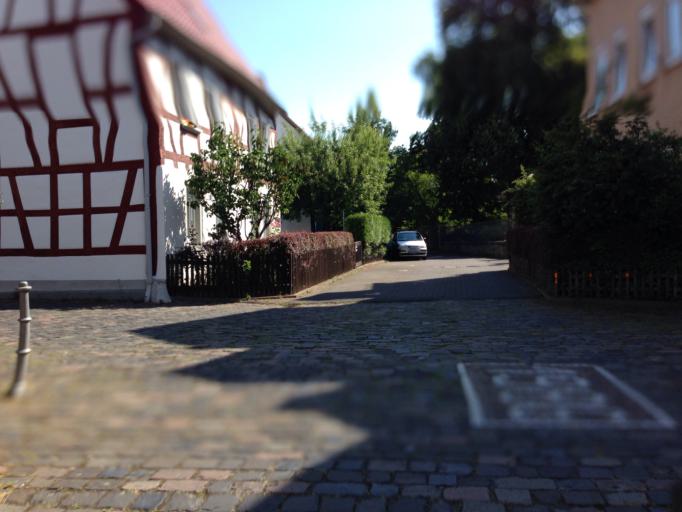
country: DE
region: Hesse
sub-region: Regierungsbezirk Darmstadt
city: Hanau am Main
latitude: 50.1287
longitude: 8.8948
